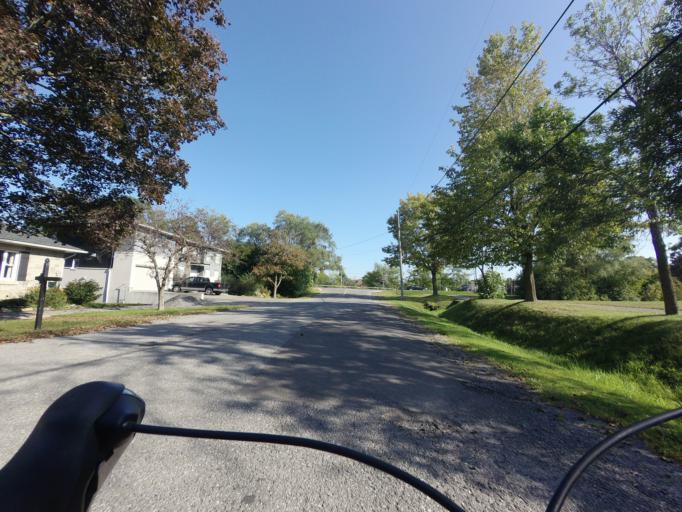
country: CA
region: Ontario
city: Bells Corners
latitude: 45.2314
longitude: -75.6814
